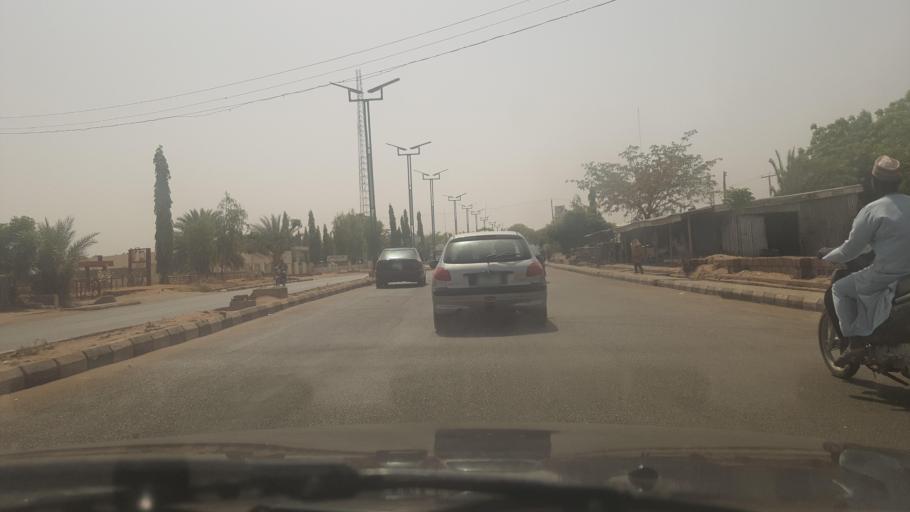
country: NG
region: Gombe
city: Gombe
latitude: 10.2865
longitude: 11.1364
